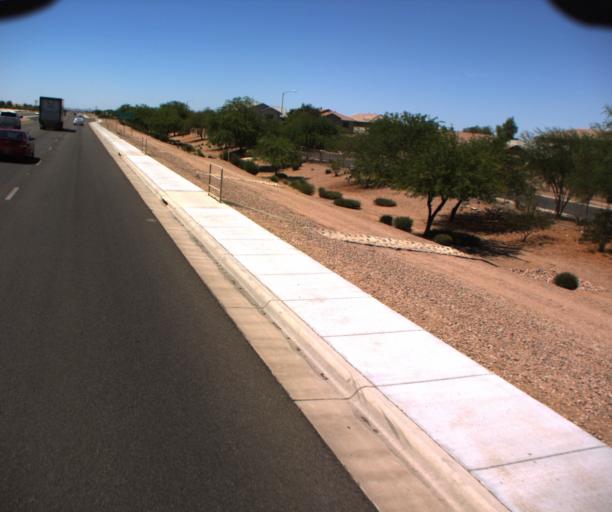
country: US
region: Arizona
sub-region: Pinal County
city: Maricopa
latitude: 33.0425
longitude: -112.0480
